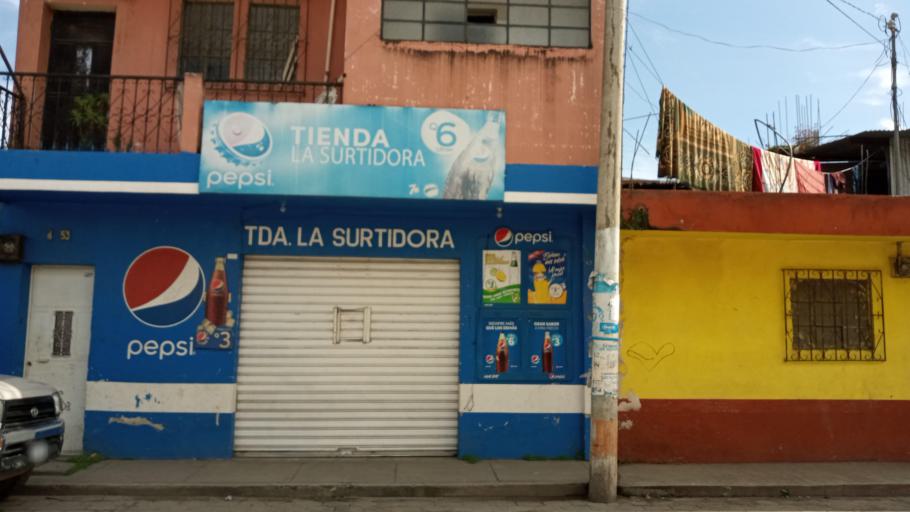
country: GT
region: Quetzaltenango
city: Quetzaltenango
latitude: 14.8421
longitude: -91.5064
